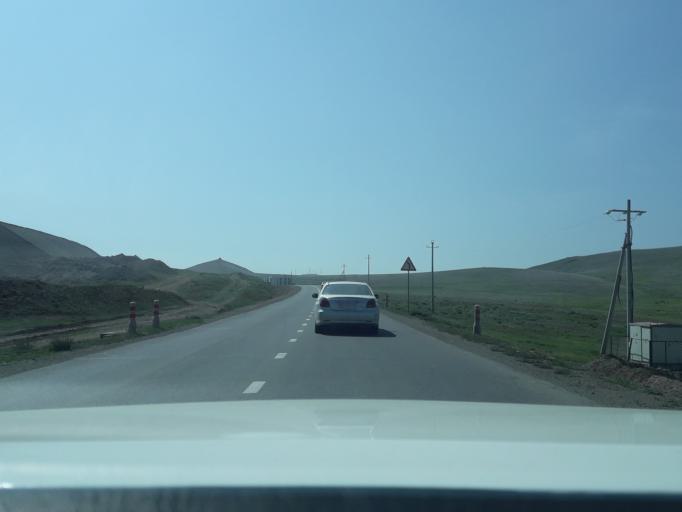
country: MN
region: Ulaanbaatar
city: Ulaanbaatar
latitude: 47.7958
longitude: 106.7454
